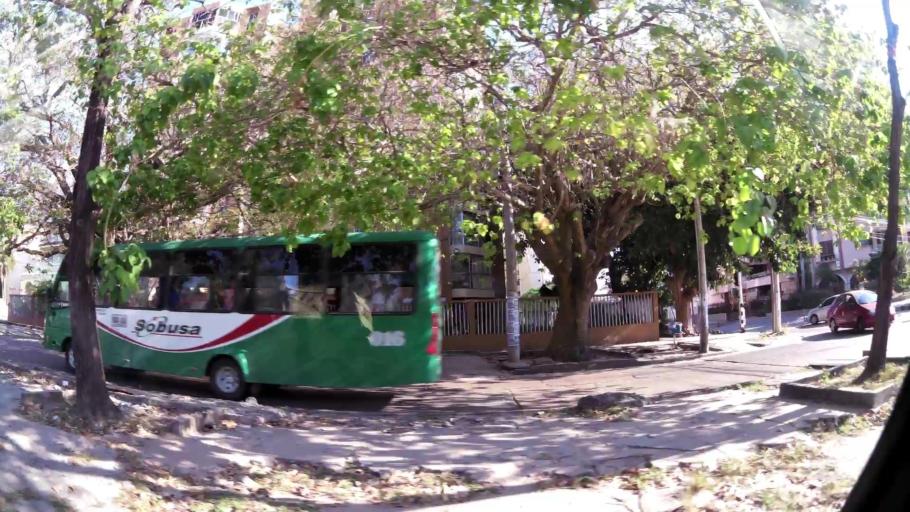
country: CO
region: Atlantico
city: Barranquilla
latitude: 10.9971
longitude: -74.7977
